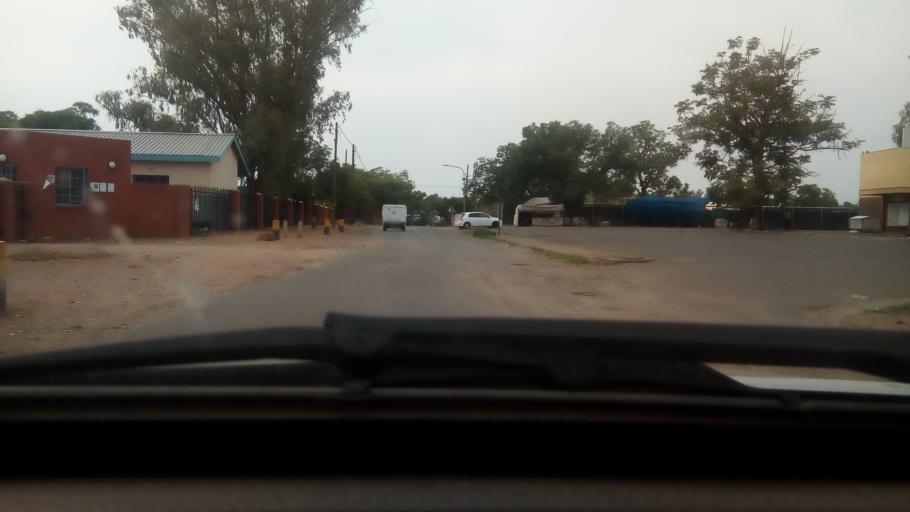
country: BW
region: South East
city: Gaborone
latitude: -24.6670
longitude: 25.9410
